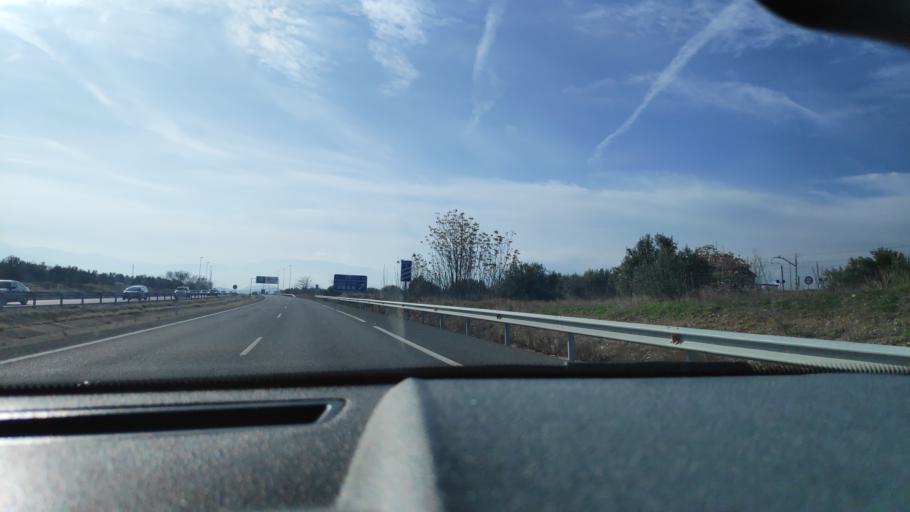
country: ES
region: Andalusia
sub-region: Provincia de Jaen
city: Jaen
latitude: 37.8288
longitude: -3.7662
